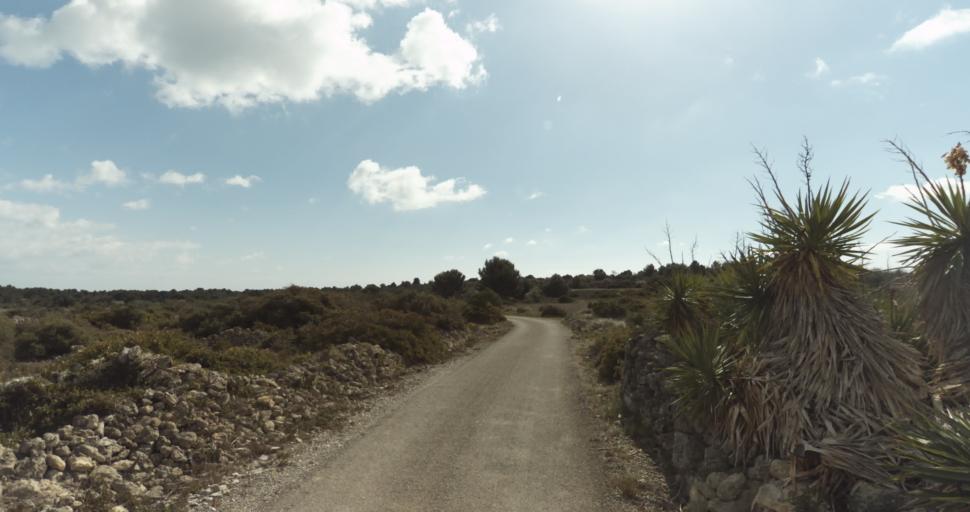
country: FR
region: Languedoc-Roussillon
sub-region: Departement de l'Aude
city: Leucate
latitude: 42.9191
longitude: 3.0398
